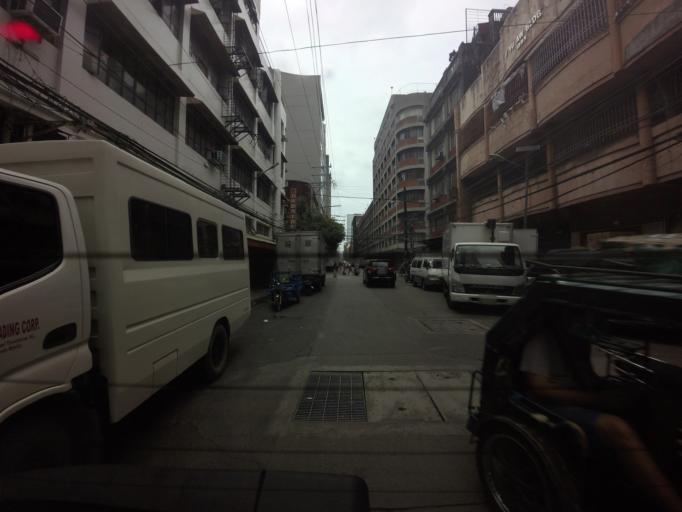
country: PH
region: Metro Manila
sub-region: City of Manila
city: Manila
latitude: 14.6008
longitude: 120.9697
